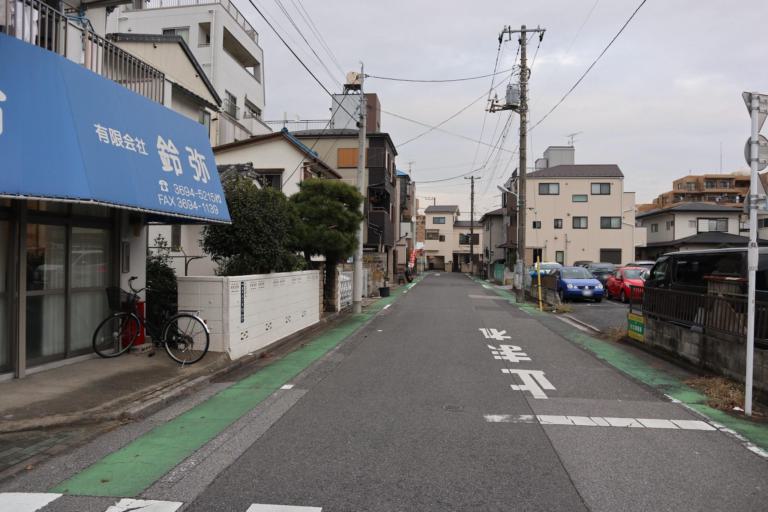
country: JP
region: Chiba
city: Matsudo
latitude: 35.7337
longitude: 139.8687
